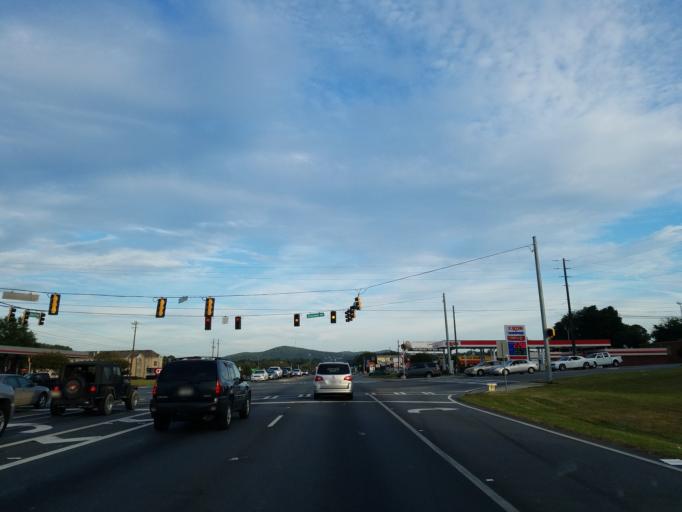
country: US
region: Georgia
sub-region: Bartow County
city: Cartersville
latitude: 34.2070
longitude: -84.8199
